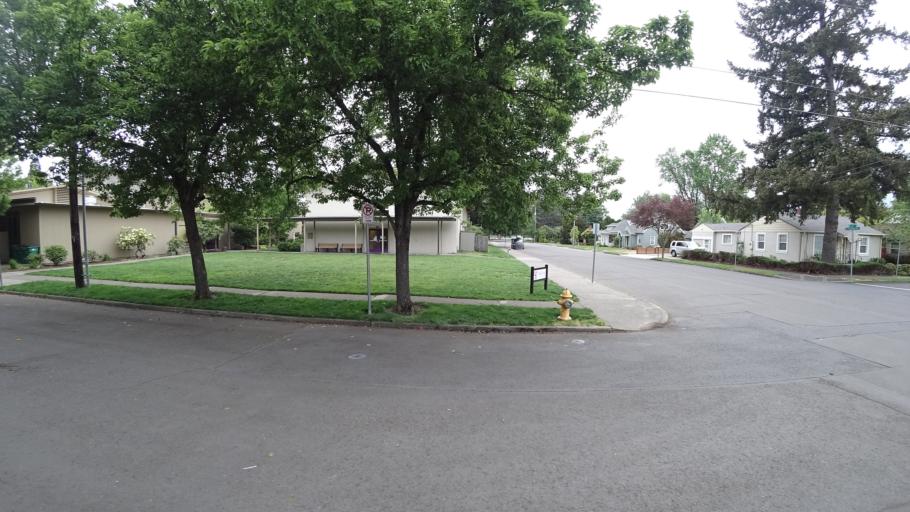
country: US
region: Oregon
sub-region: Washington County
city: Beaverton
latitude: 45.4821
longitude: -122.8063
